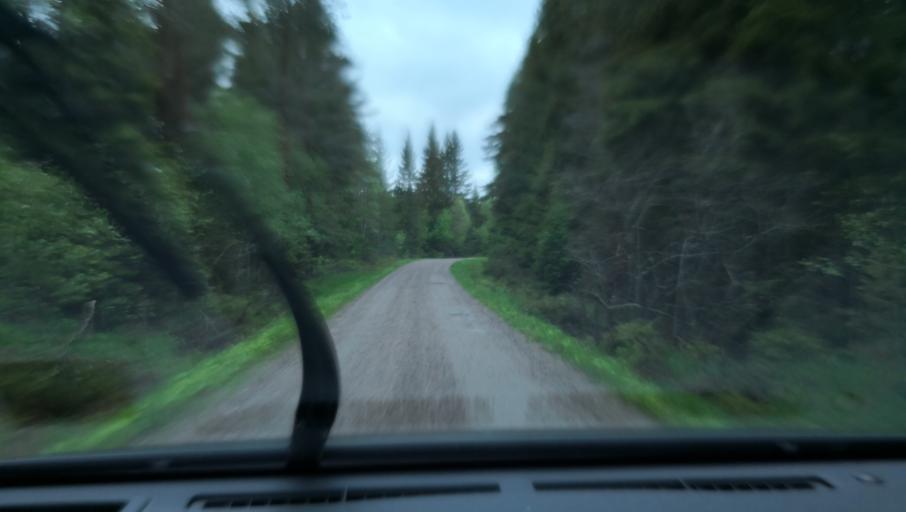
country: SE
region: Uppsala
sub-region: Heby Kommun
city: OEstervala
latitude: 59.9872
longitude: 17.2595
